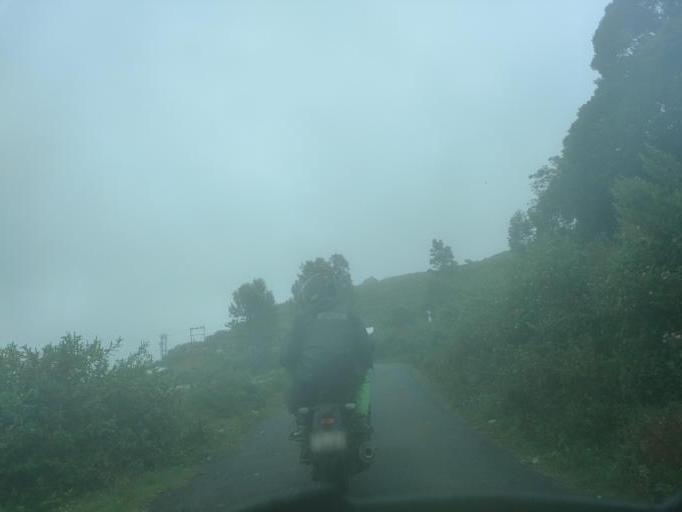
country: IN
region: Tamil Nadu
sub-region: Dindigul
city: Kodaikanal
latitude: 10.2336
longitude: 77.3295
